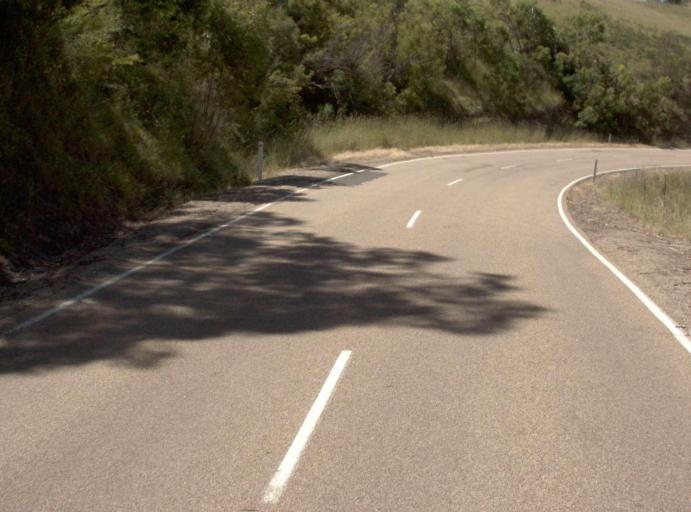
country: AU
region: Victoria
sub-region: East Gippsland
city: Lakes Entrance
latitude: -37.4856
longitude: 148.1871
